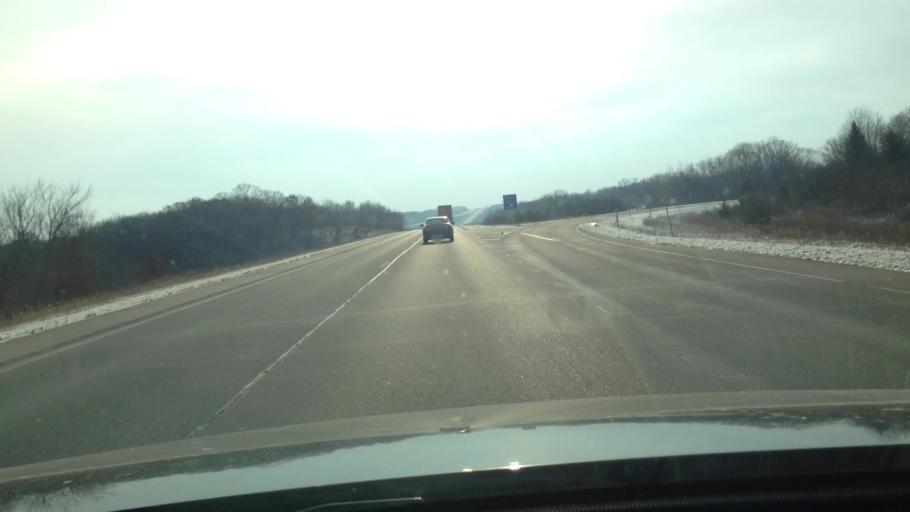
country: US
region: Wisconsin
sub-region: Walworth County
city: East Troy
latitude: 42.7368
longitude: -88.4570
